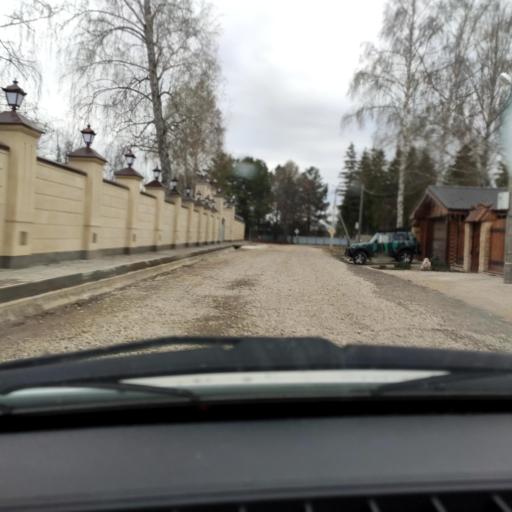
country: RU
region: Bashkortostan
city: Ufa
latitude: 54.7820
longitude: 56.1807
